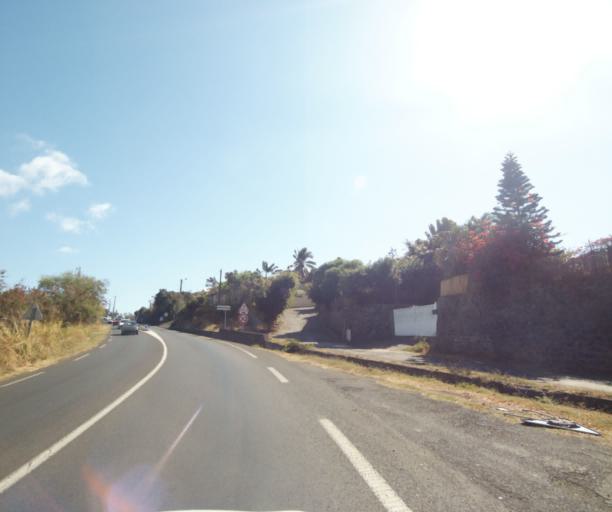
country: RE
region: Reunion
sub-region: Reunion
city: Le Port
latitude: -20.9808
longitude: 55.3174
